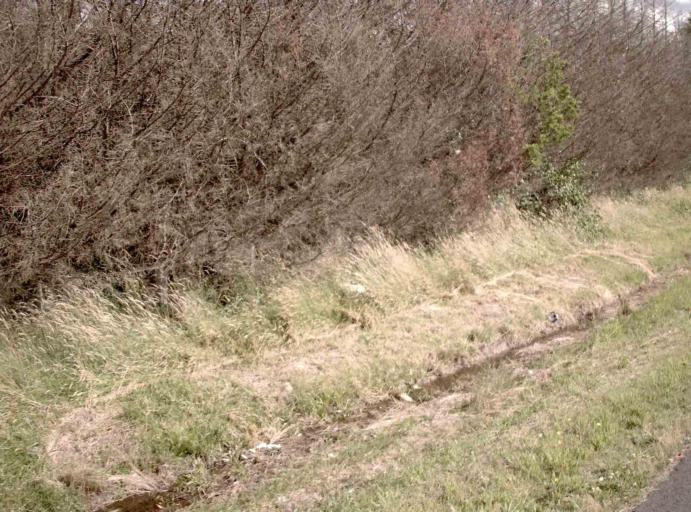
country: AU
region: Victoria
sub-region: Latrobe
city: Morwell
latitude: -38.2956
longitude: 146.4233
